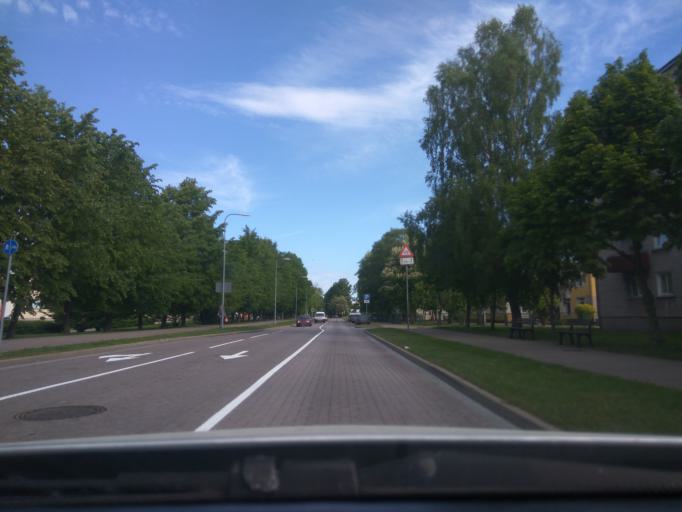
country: LV
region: Ventspils
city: Ventspils
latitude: 57.3927
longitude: 21.5734
